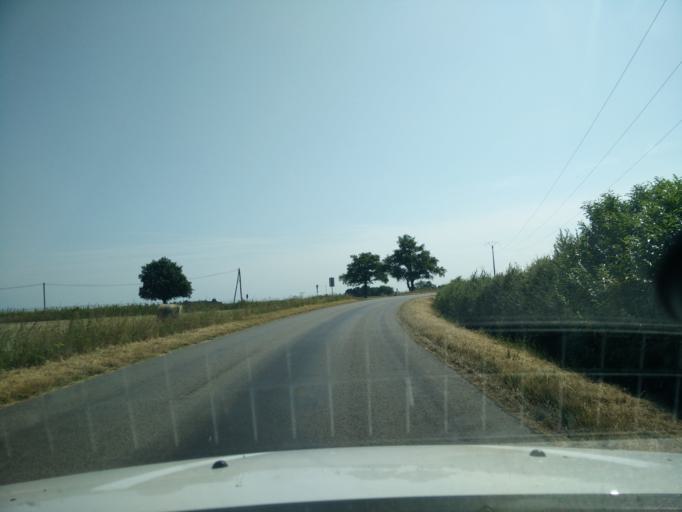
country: FR
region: Auvergne
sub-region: Departement de l'Allier
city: Neuvy
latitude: 46.4803
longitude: 3.2857
